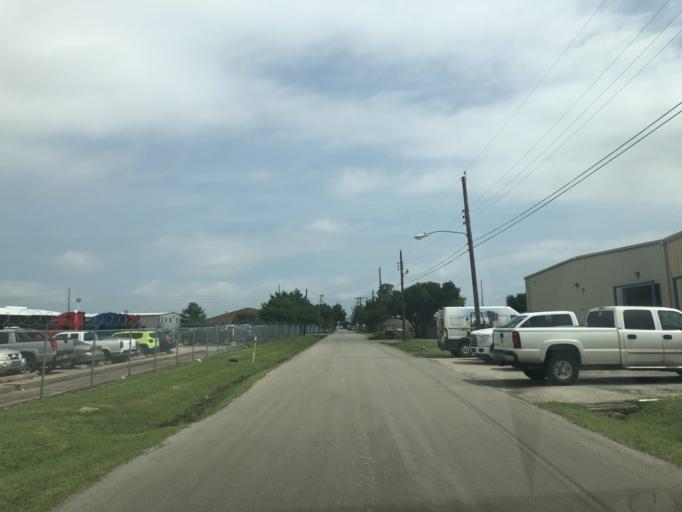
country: US
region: Texas
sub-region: Dallas County
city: Cockrell Hill
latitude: 32.8029
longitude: -96.8800
